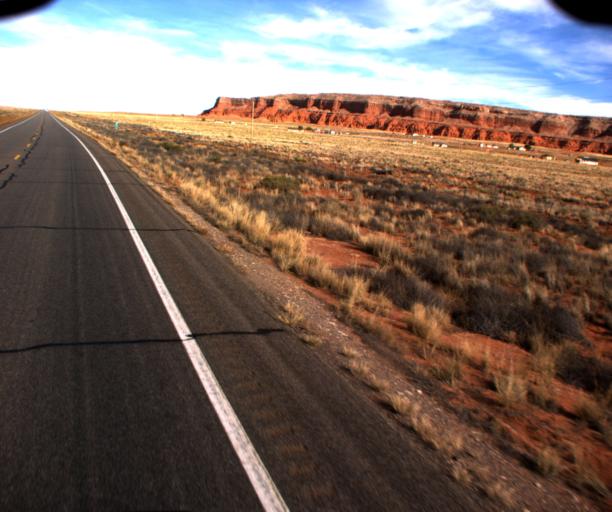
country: US
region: Arizona
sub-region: Navajo County
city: Kayenta
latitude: 36.7877
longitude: -109.9552
